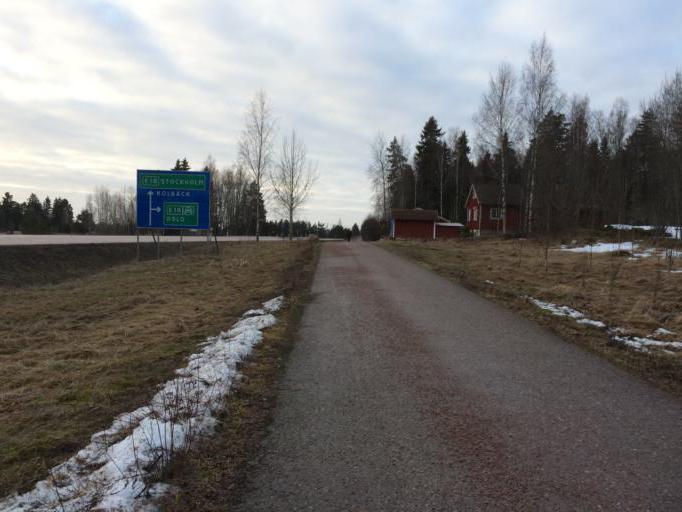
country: SE
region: Vaestmanland
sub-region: Hallstahammars Kommun
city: Hallstahammar
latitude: 59.5967
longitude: 16.2491
